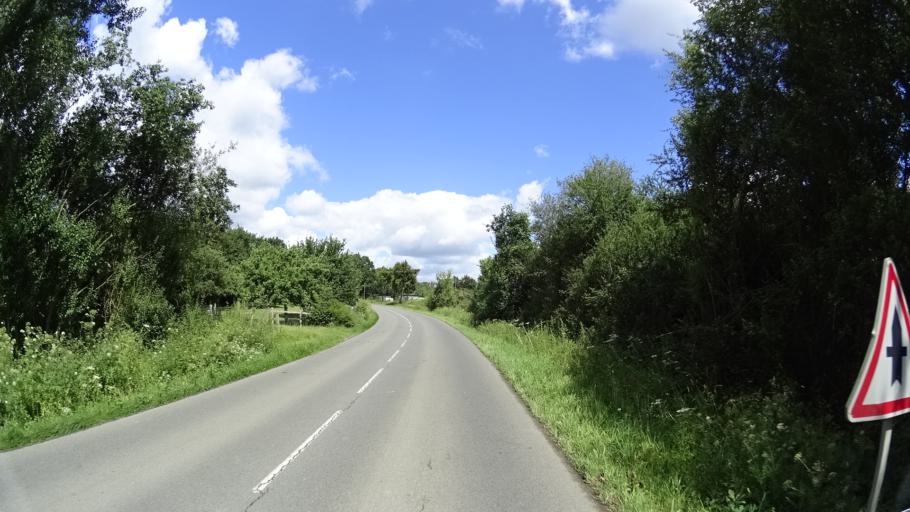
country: FR
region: Brittany
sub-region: Departement d'Ille-et-Vilaine
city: Saint-Gilles
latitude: 48.1361
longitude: -1.8257
